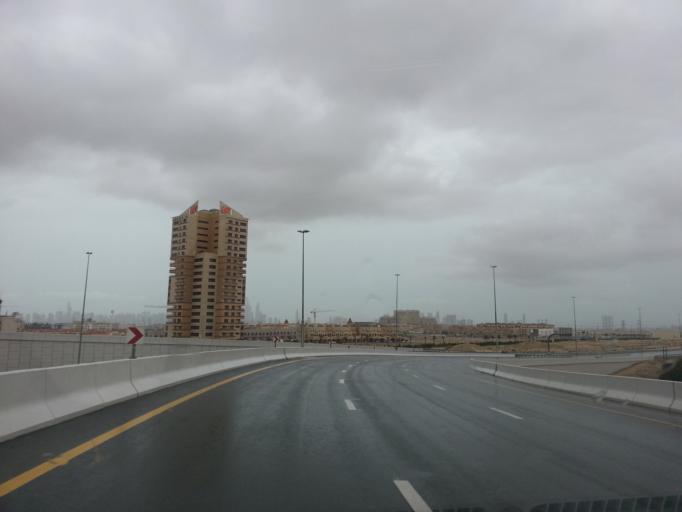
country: AE
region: Dubai
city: Dubai
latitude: 25.0553
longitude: 55.2236
